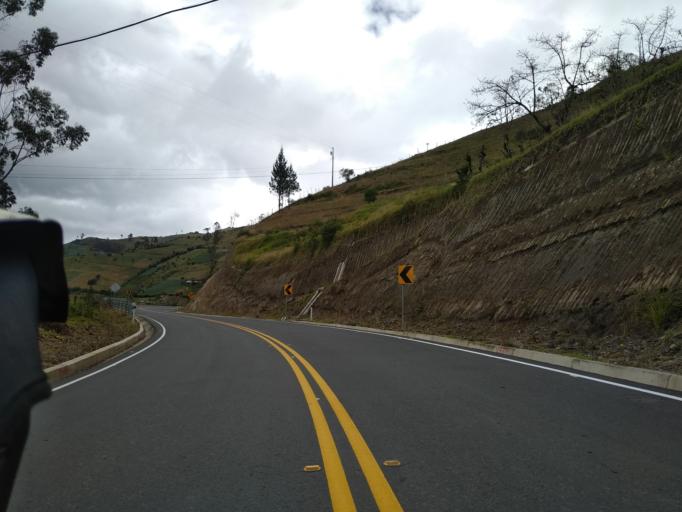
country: EC
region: Cotopaxi
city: Saquisili
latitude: -0.7531
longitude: -78.9083
